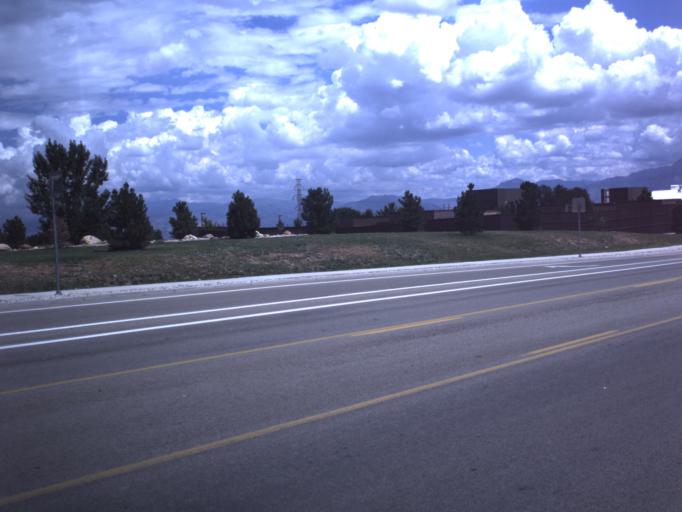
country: US
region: Utah
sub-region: Salt Lake County
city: Oquirrh
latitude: 40.5877
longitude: -112.0349
